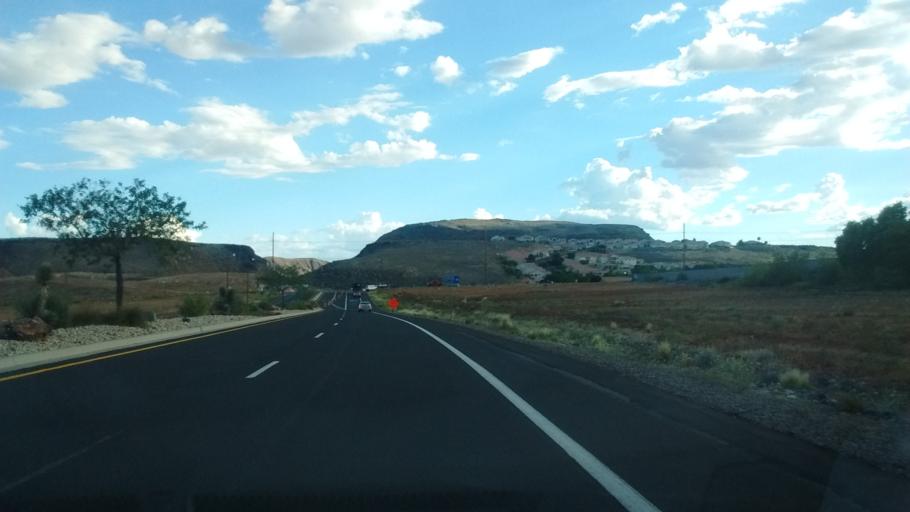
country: US
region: Utah
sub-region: Washington County
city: Washington
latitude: 37.1339
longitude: -113.4857
